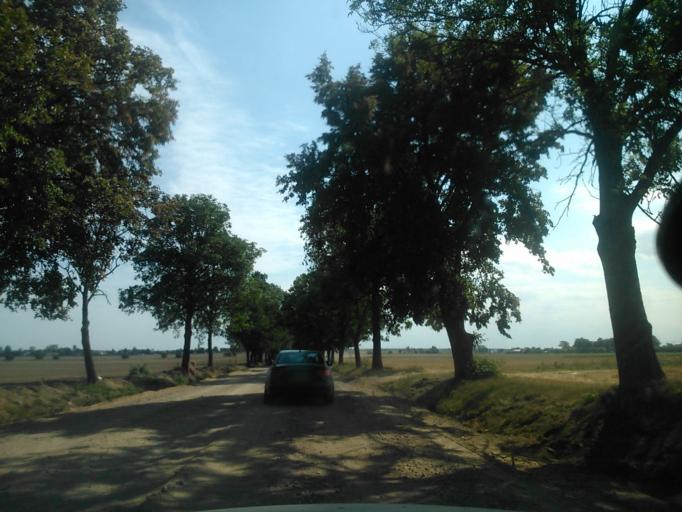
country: PL
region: Warmian-Masurian Voivodeship
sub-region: Powiat dzialdowski
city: Dzialdowo
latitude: 53.2134
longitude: 20.2238
